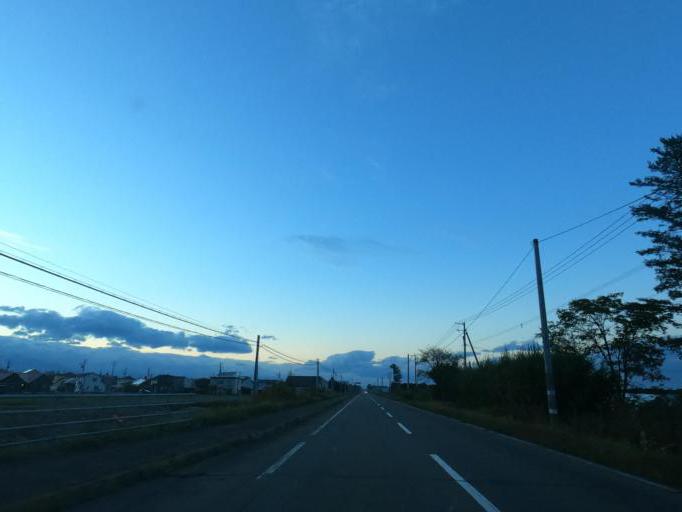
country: JP
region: Hokkaido
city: Obihiro
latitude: 42.6463
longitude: 143.1975
